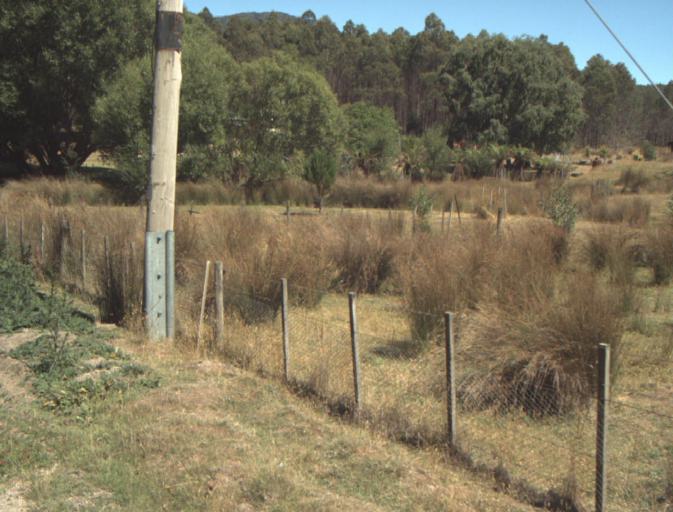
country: AU
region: Tasmania
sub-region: Dorset
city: Scottsdale
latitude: -41.2732
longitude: 147.3470
